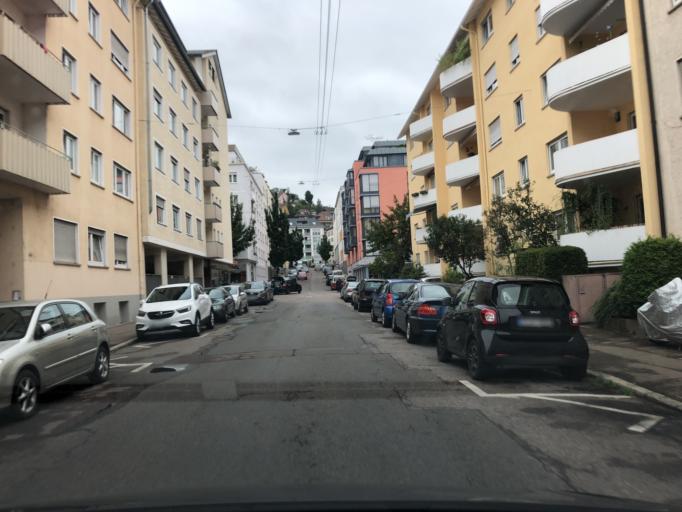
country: DE
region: Baden-Wuerttemberg
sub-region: Regierungsbezirk Stuttgart
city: Stuttgart
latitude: 48.7823
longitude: 9.1605
